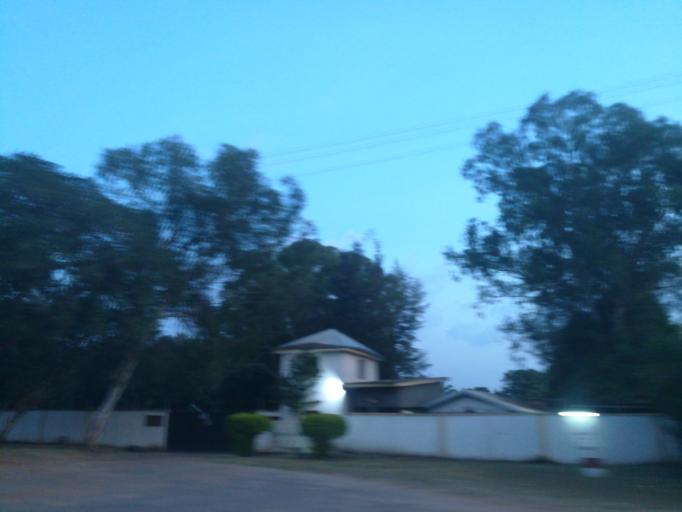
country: NG
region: Abuja Federal Capital Territory
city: Abuja
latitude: 9.0744
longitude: 7.4065
